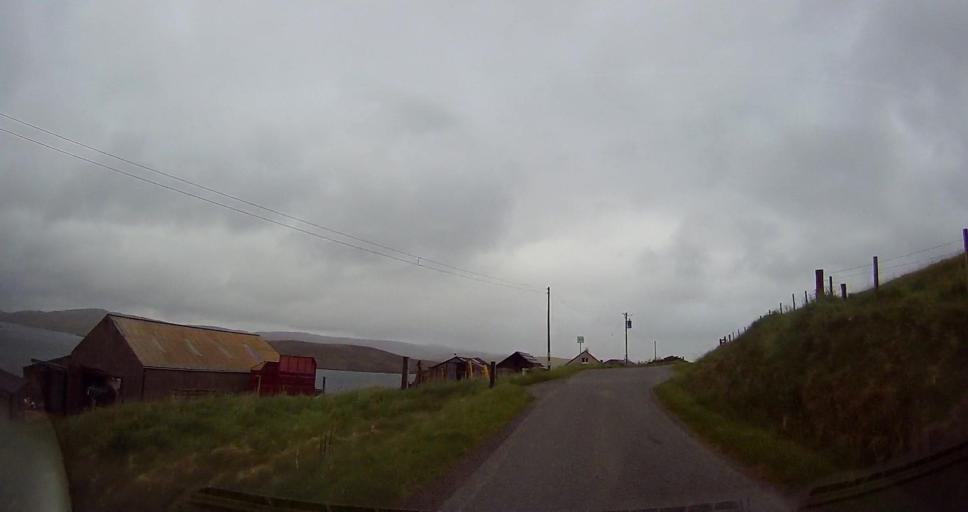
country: GB
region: Scotland
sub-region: Shetland Islands
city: Lerwick
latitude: 60.3708
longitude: -1.3826
